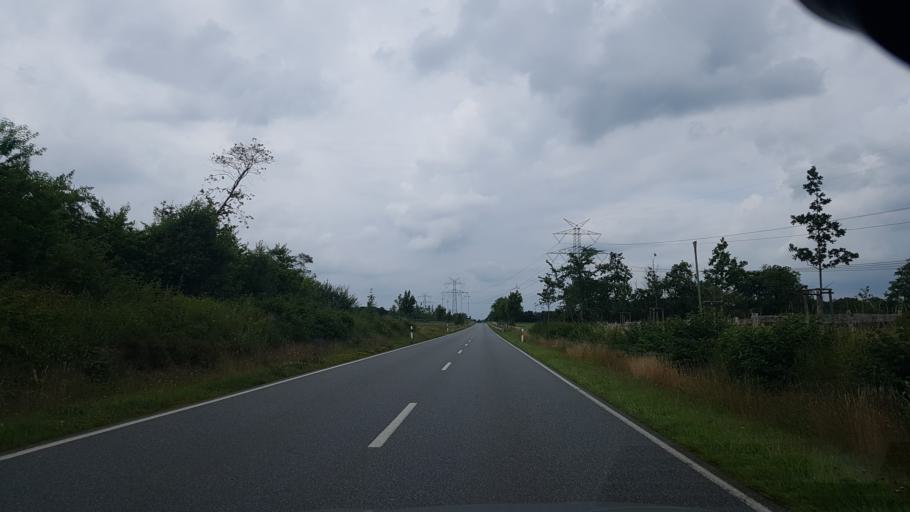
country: DE
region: Schleswig-Holstein
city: Jardelund
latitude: 54.8266
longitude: 9.2189
